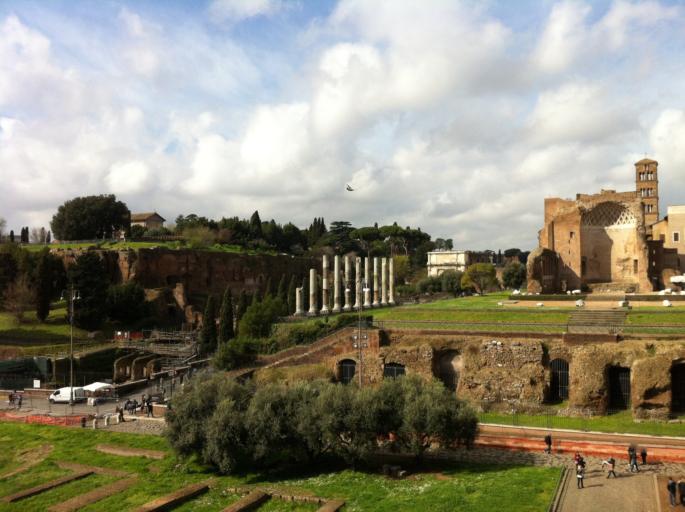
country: IT
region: Latium
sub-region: Citta metropolitana di Roma Capitale
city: Rome
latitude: 41.8905
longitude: 12.4915
